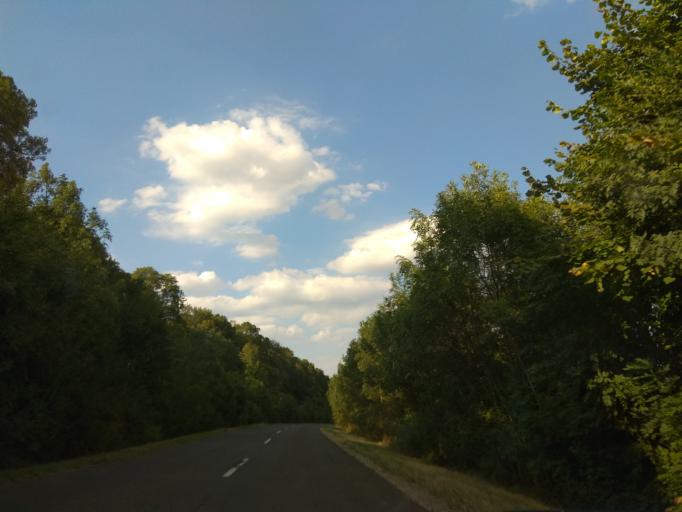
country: HU
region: Borsod-Abauj-Zemplen
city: Harsany
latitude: 47.9294
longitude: 20.7280
